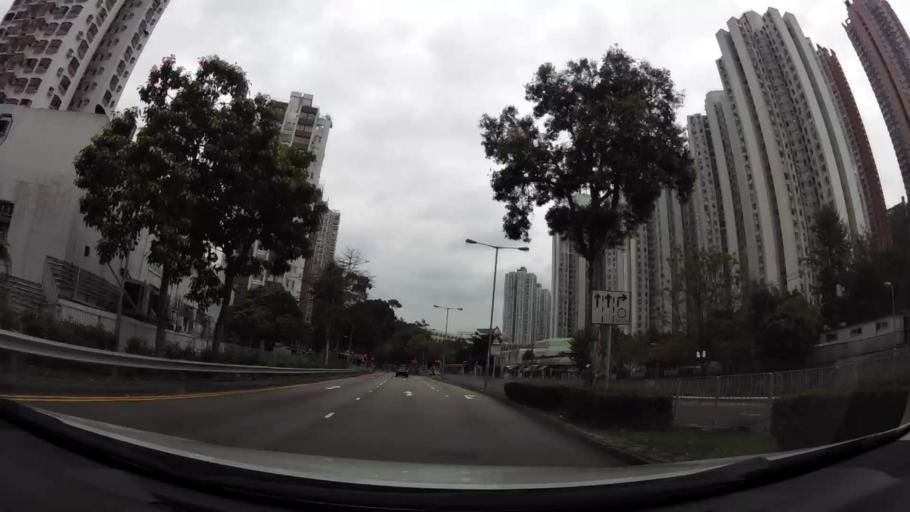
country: HK
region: Tuen Mun
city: Tuen Mun
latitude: 22.4023
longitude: 113.9788
